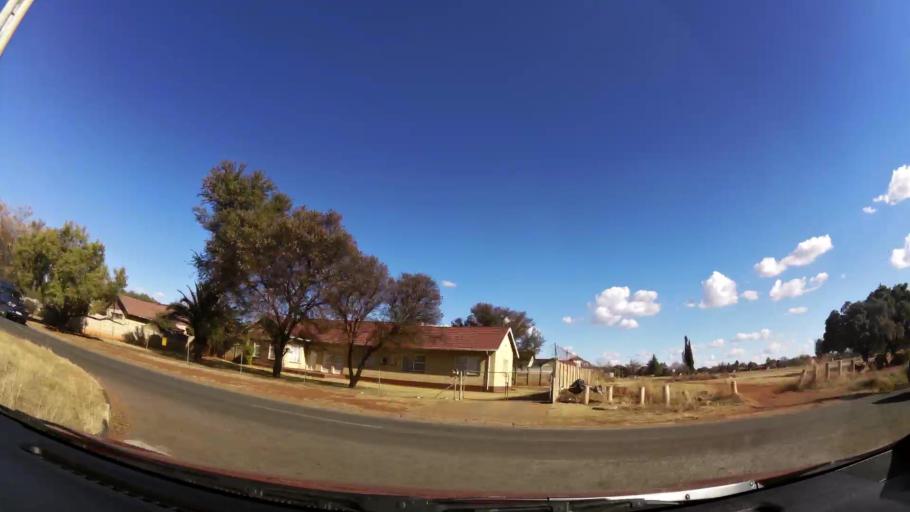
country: ZA
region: Gauteng
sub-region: West Rand District Municipality
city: Carletonville
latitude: -26.3616
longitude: 27.3699
